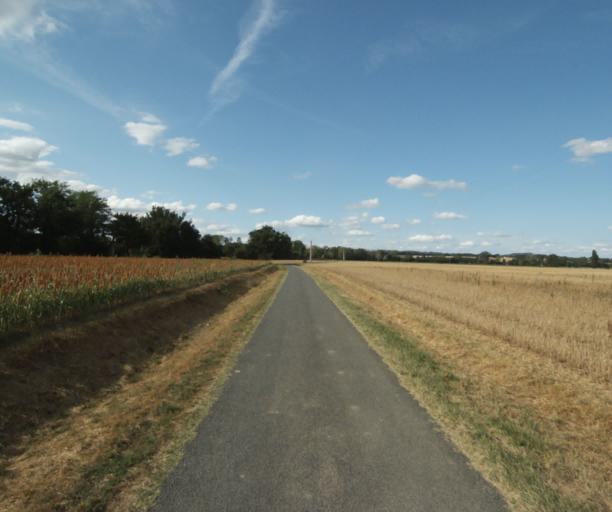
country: FR
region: Midi-Pyrenees
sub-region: Departement de la Haute-Garonne
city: Revel
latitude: 43.5158
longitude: 1.9906
